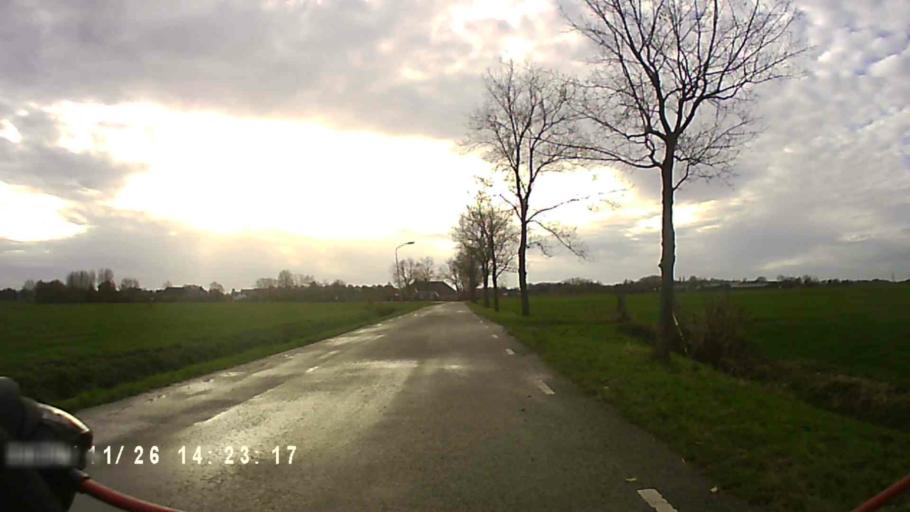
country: NL
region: Groningen
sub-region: Gemeente Appingedam
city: Appingedam
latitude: 53.3303
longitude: 6.8652
